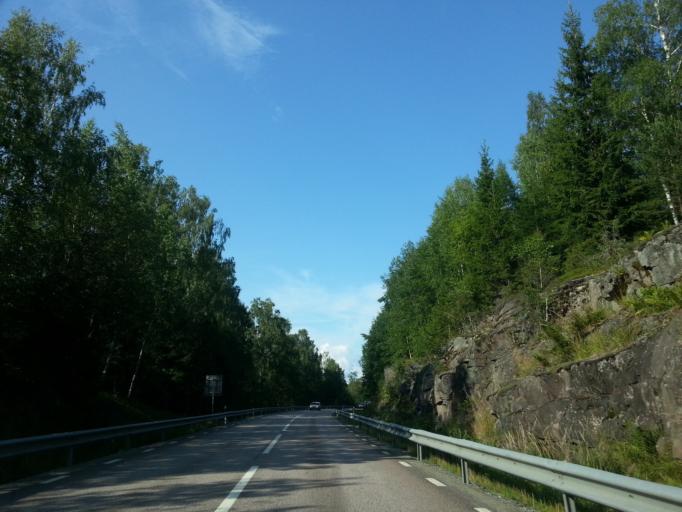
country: SE
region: Vaestmanland
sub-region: Skinnskattebergs Kommun
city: Skinnskatteberg
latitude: 59.8839
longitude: 15.6704
